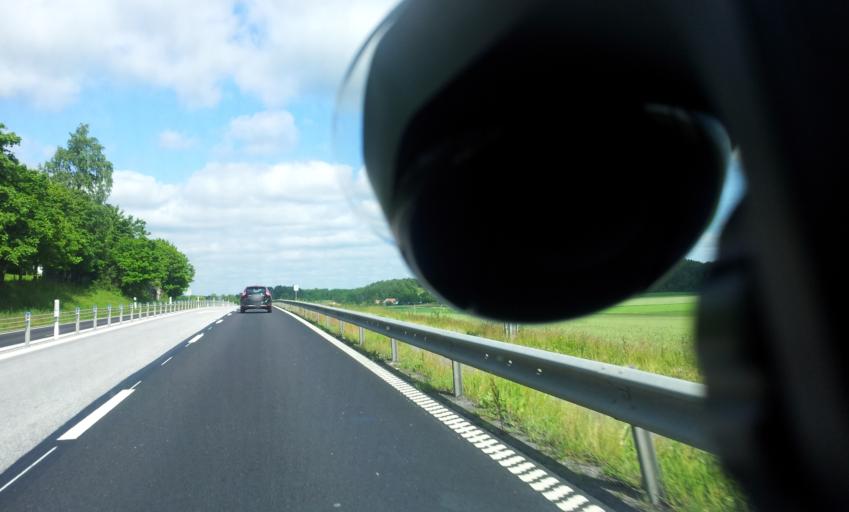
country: SE
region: OEstergoetland
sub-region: Soderkopings Kommun
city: Soederkoeping
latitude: 58.5393
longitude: 16.2772
